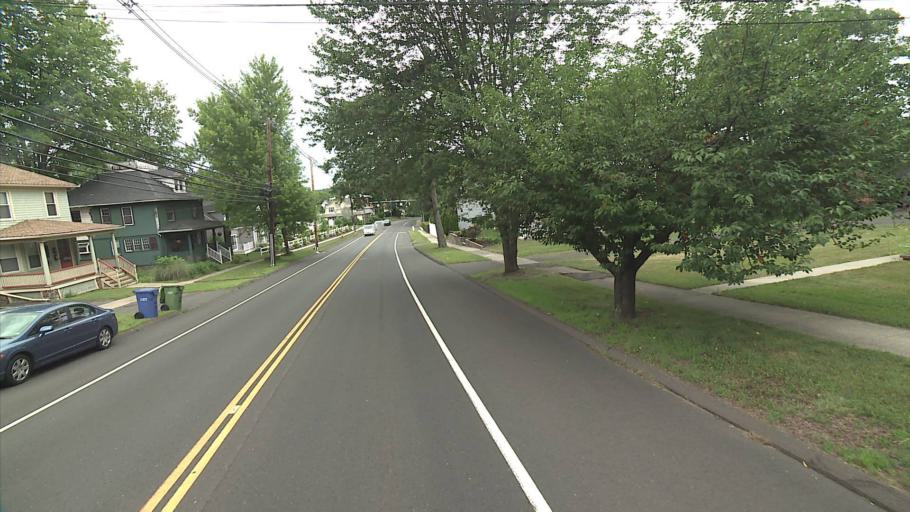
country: US
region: Connecticut
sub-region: New Haven County
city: Wallingford Center
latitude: 41.4495
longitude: -72.8088
